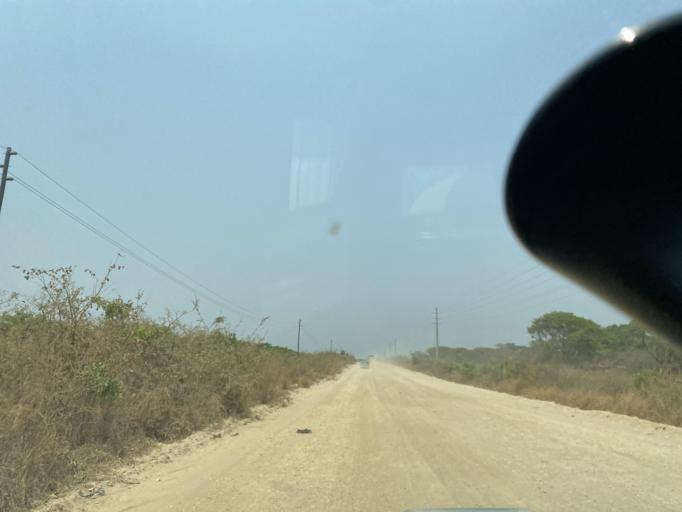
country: ZM
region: Lusaka
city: Lusaka
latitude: -15.5337
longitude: 28.3449
